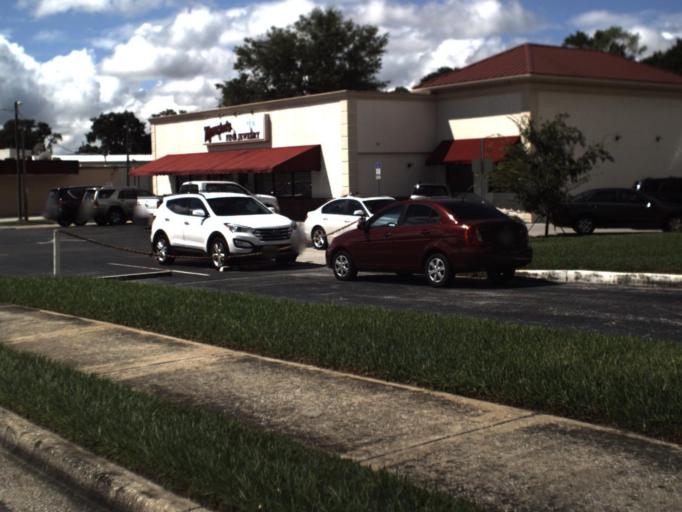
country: US
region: Florida
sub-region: Polk County
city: Lakeland
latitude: 28.0060
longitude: -81.9571
